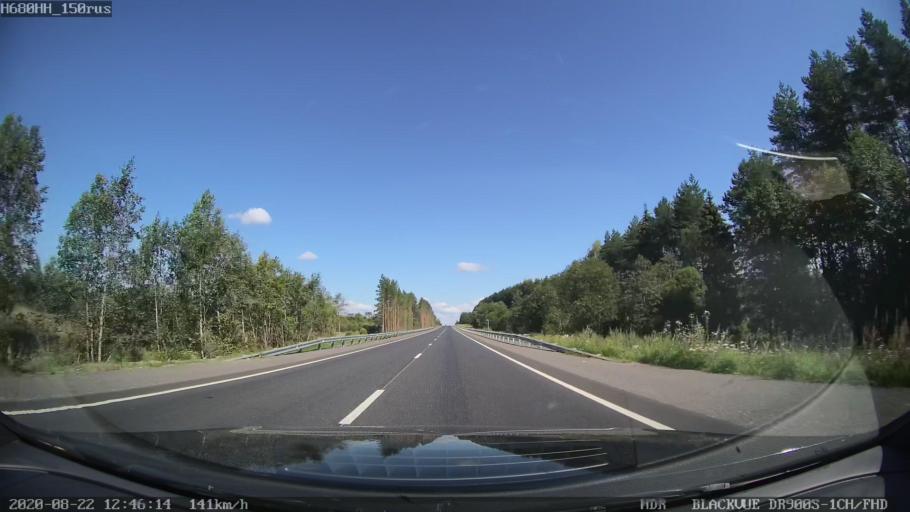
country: RU
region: Tverskaya
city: Rameshki
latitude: 57.4166
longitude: 36.1407
